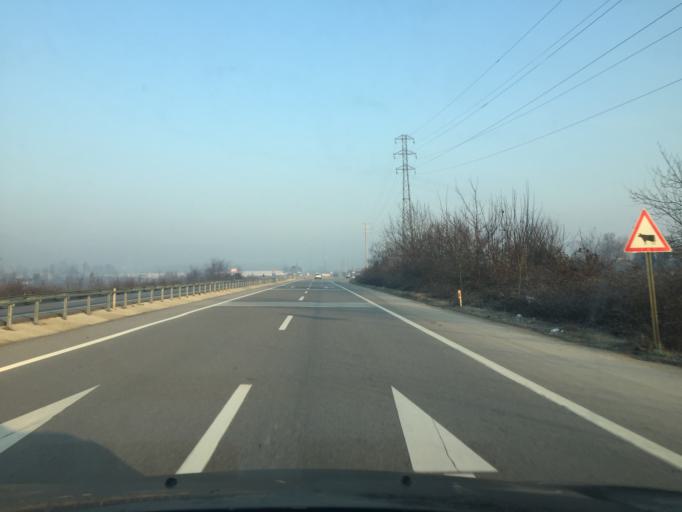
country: TR
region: Sakarya
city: Akyazi
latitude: 40.7094
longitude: 30.5653
